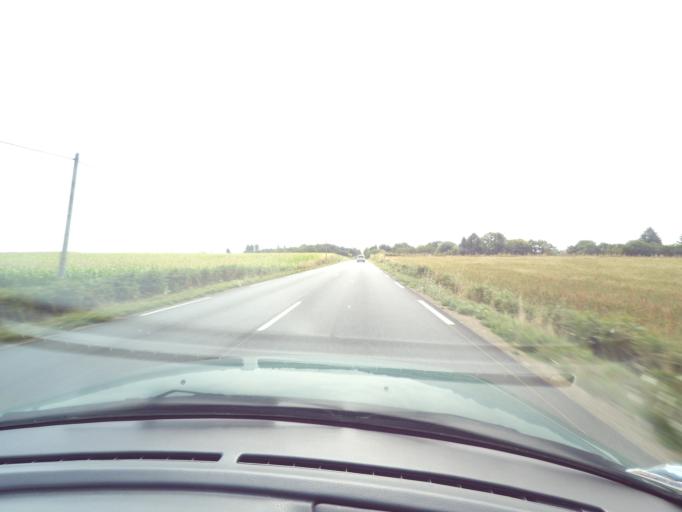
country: FR
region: Limousin
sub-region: Departement de la Haute-Vienne
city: Neuvic-Entier
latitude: 45.7477
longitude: 1.6006
